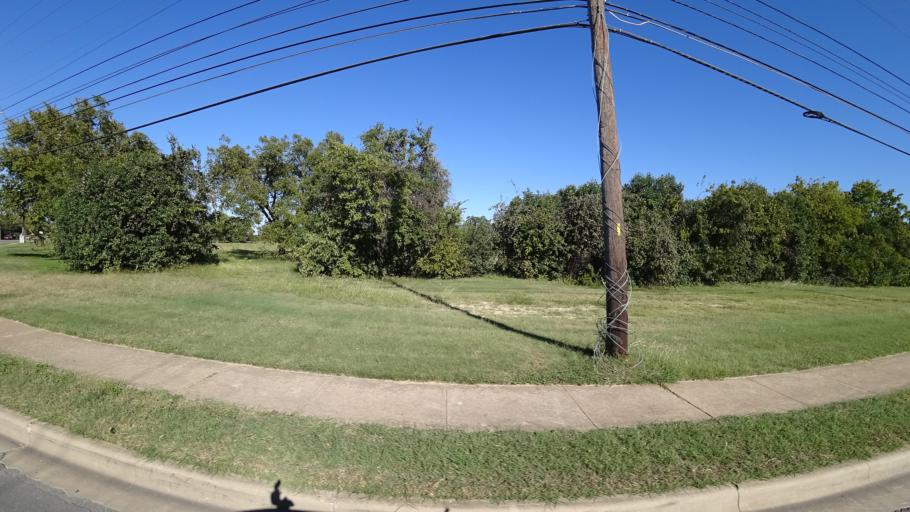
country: US
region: Texas
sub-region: Travis County
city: West Lake Hills
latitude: 30.3175
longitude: -97.7551
